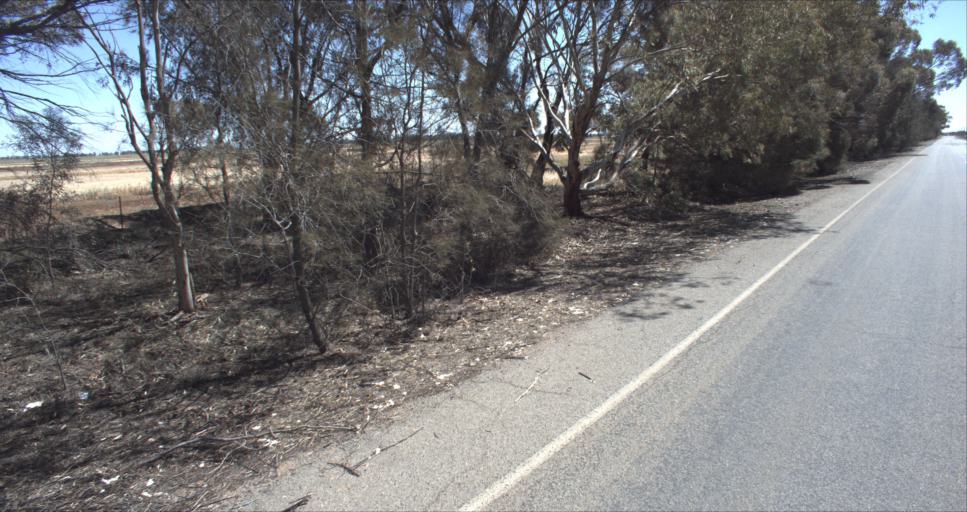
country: AU
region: New South Wales
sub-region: Leeton
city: Leeton
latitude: -34.4699
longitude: 146.2925
